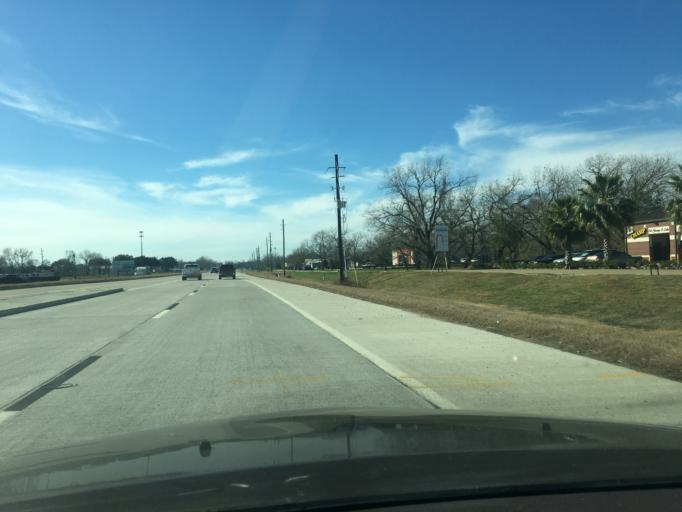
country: US
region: Texas
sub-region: Fort Bend County
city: Richmond
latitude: 29.5919
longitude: -95.7453
